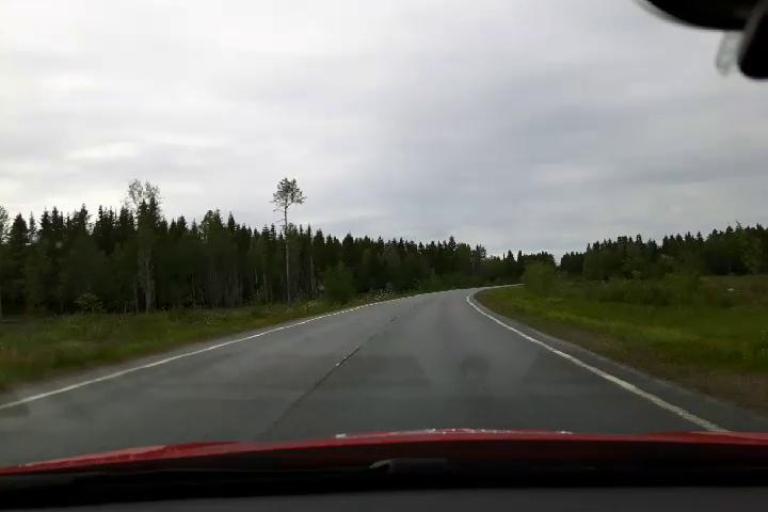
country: SE
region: Jaemtland
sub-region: Bergs Kommun
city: Hoverberg
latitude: 62.9070
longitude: 14.3324
